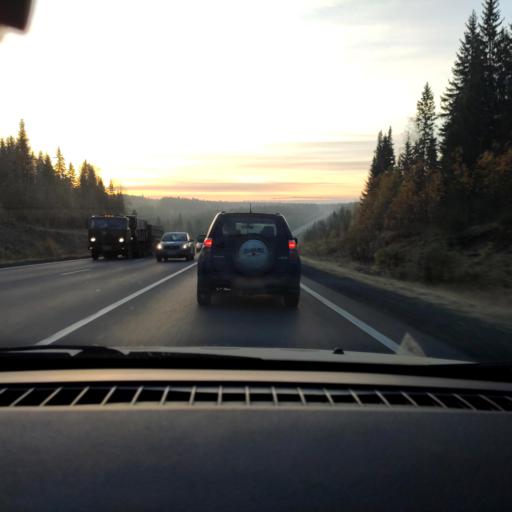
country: RU
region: Perm
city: Novyye Lyady
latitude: 58.0402
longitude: 56.4602
